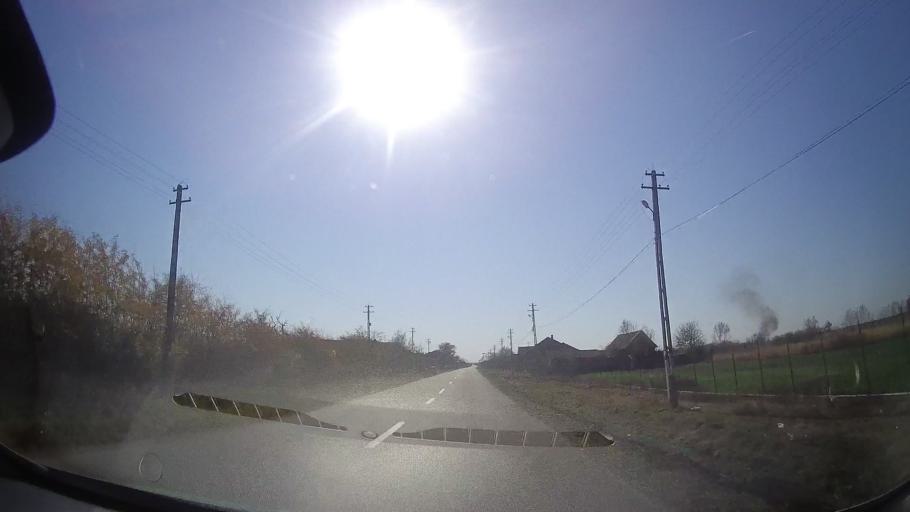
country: RO
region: Timis
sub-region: Comuna Ghizela
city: Ghizela
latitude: 45.7966
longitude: 21.7270
